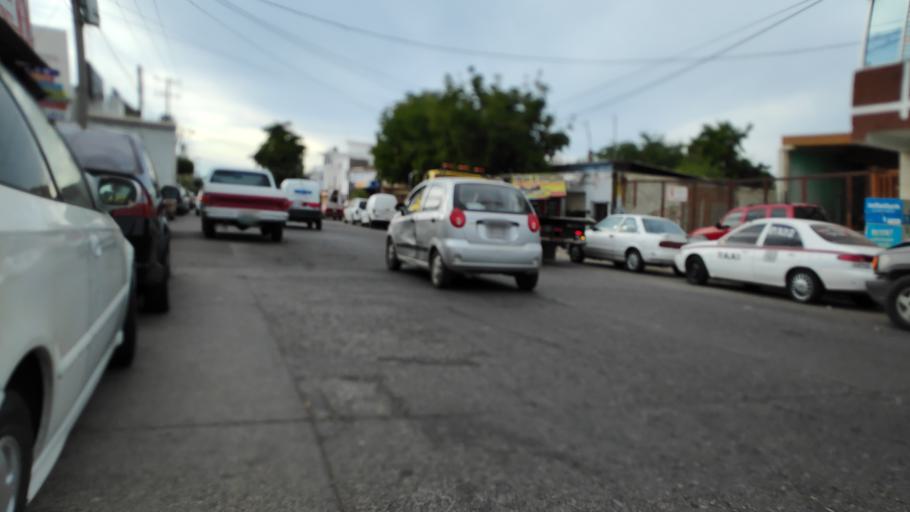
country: MX
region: Sinaloa
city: Culiacan
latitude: 24.8018
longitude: -107.3915
